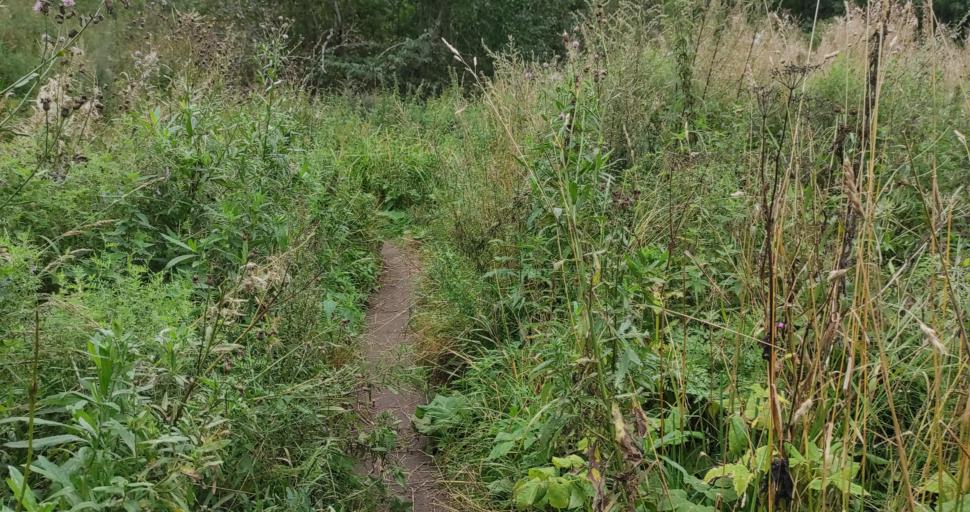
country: RU
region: Leningrad
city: Kuznechnoye
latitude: 61.1749
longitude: 29.6940
